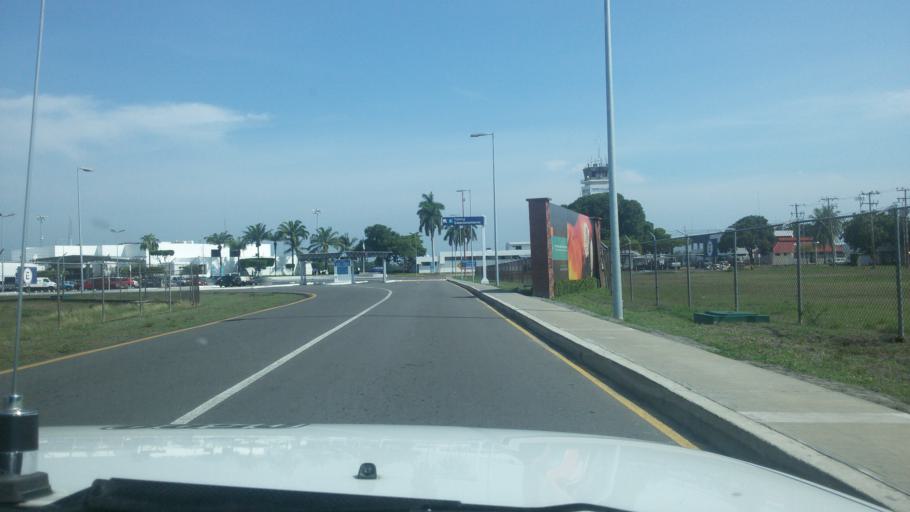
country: MX
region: Chiapas
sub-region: Tapachula
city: Congregacion Reforma
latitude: 14.7894
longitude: -92.3671
